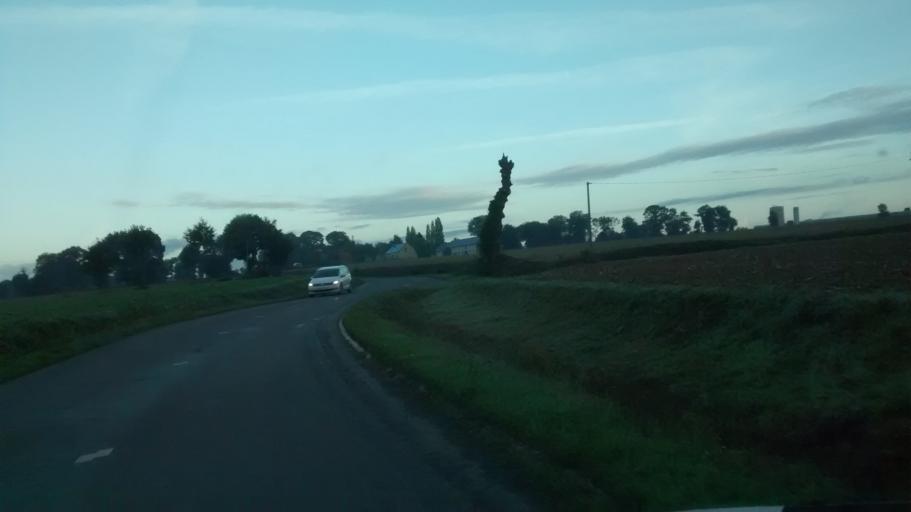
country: FR
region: Brittany
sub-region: Departement d'Ille-et-Vilaine
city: Melesse
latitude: 48.1932
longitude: -1.6784
